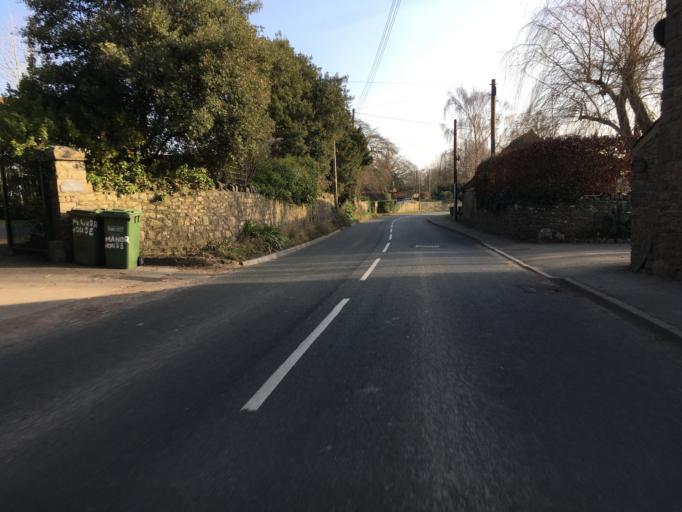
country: GB
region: England
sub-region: South Gloucestershire
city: Tytherington
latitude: 51.5925
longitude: -2.4787
